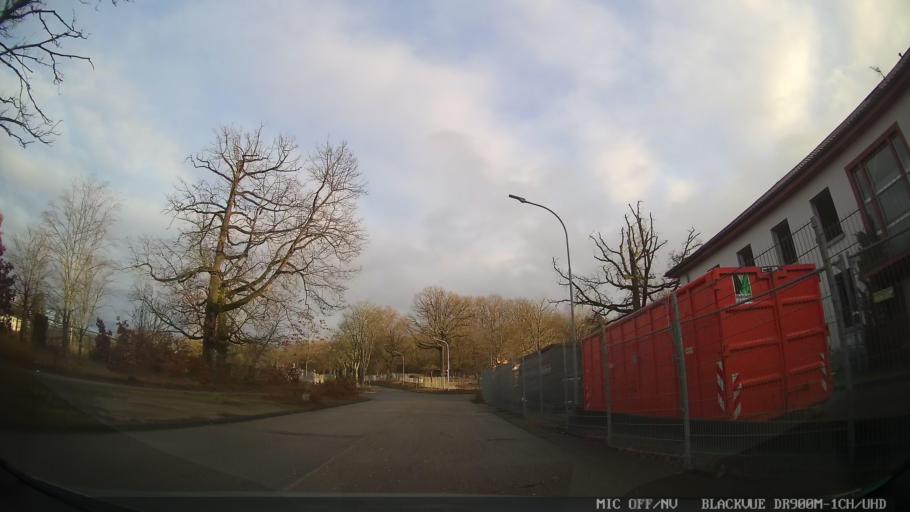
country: DE
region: Hesse
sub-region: Regierungsbezirk Darmstadt
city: Darmstadt
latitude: 49.8443
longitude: 8.6512
